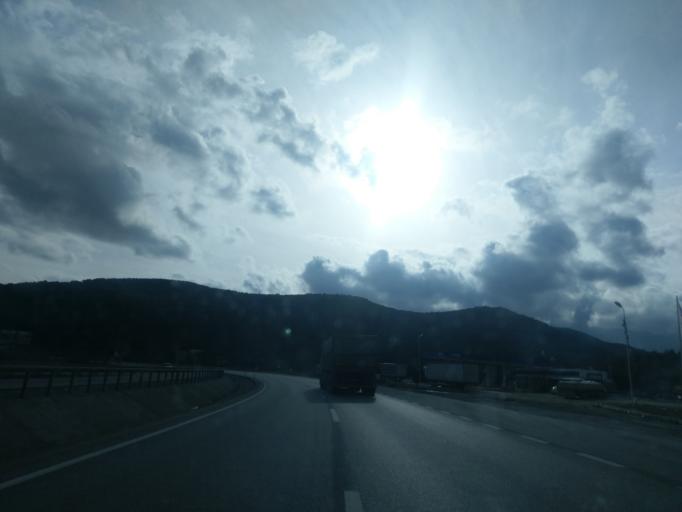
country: TR
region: Kuetahya
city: Sabuncu
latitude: 39.5685
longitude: 30.0726
